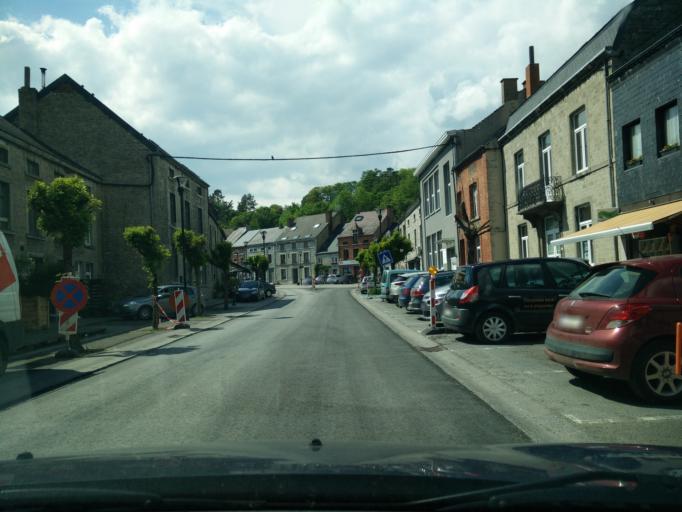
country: BE
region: Wallonia
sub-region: Province de Namur
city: Couvin
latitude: 50.0749
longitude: 4.5477
